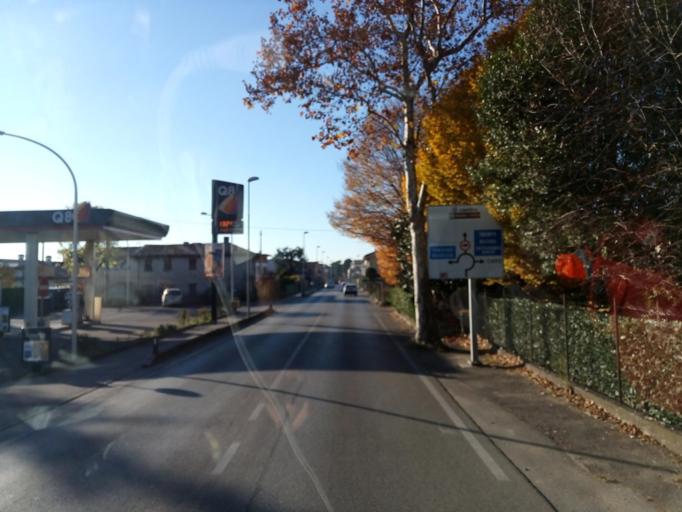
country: IT
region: Veneto
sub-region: Provincia di Treviso
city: Montebelluna
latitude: 45.7803
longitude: 12.0670
